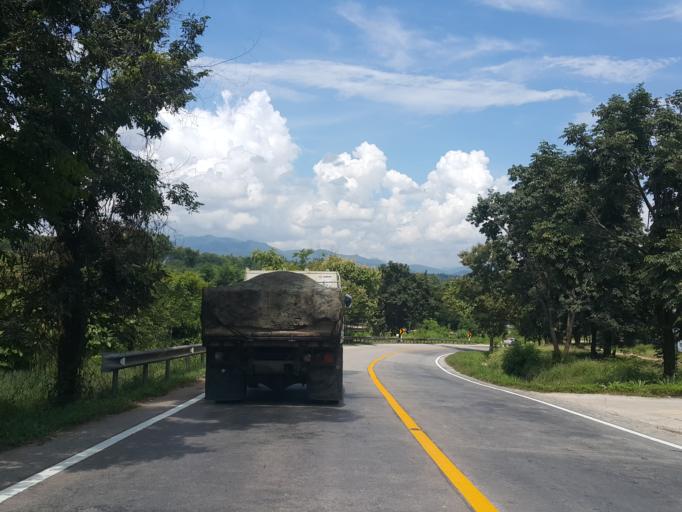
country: TH
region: Chiang Mai
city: Phrao
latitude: 19.2822
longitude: 99.1881
